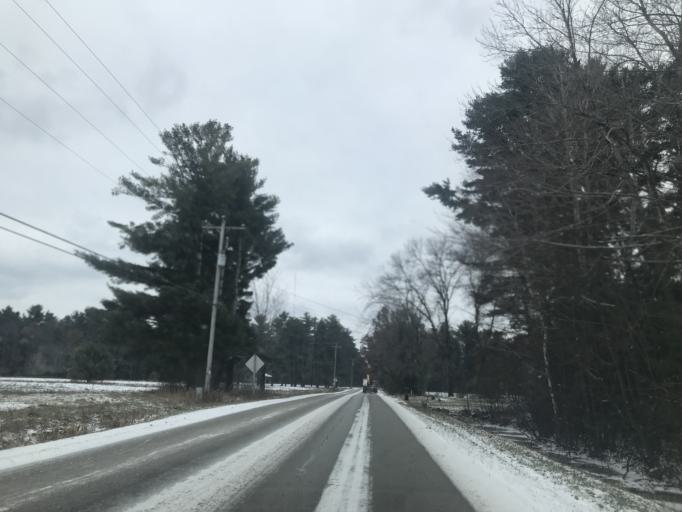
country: US
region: Wisconsin
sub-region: Marinette County
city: Marinette
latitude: 45.0697
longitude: -87.6595
